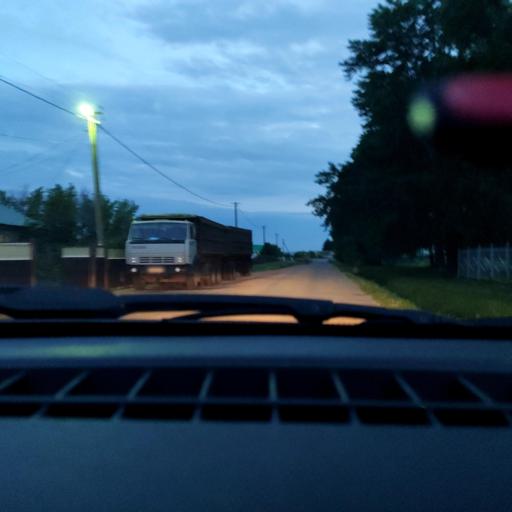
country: RU
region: Bashkortostan
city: Tolbazy
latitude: 54.2965
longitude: 55.8093
